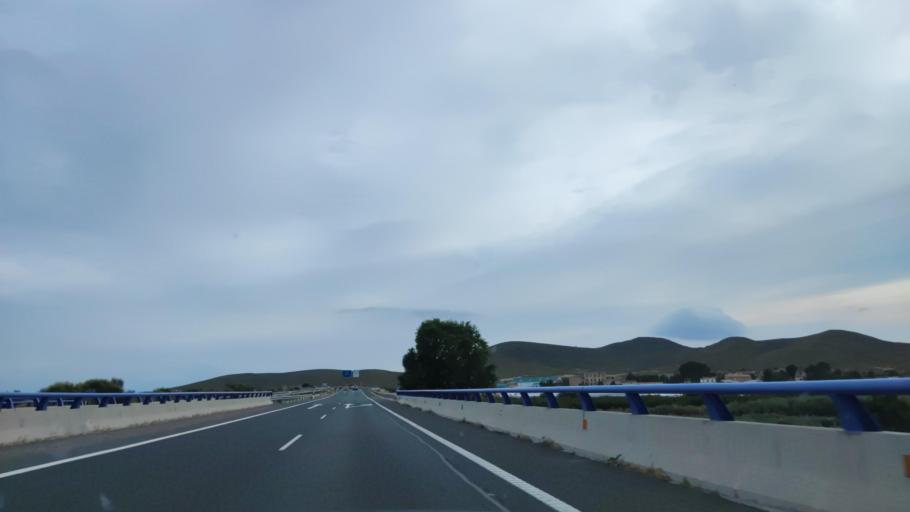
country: ES
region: Castille-La Mancha
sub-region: Provincia de Albacete
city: Tobarra
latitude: 38.5819
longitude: -1.6817
